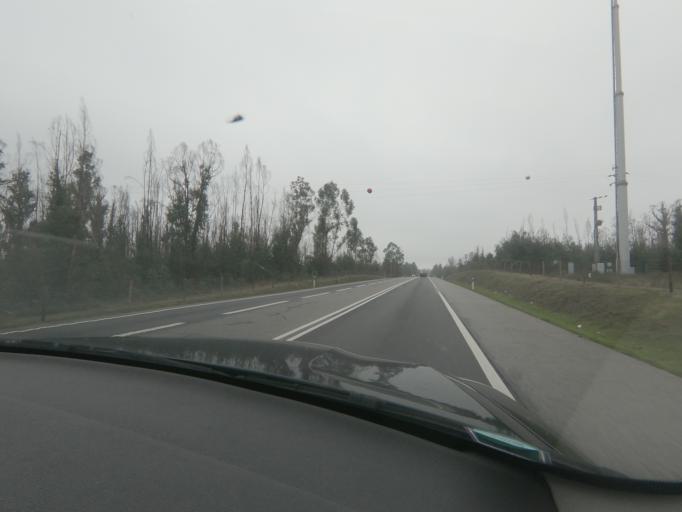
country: PT
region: Viseu
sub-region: Concelho de Tondela
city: Tondela
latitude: 40.5612
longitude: -8.0511
